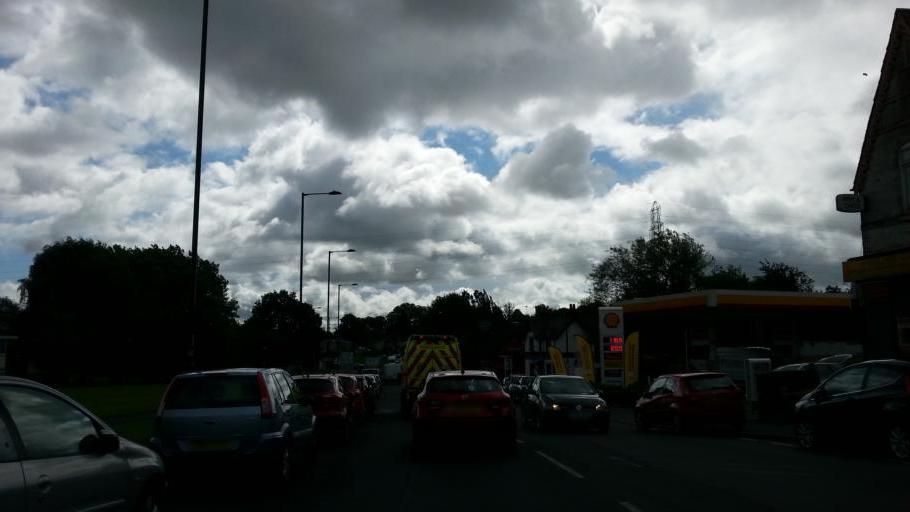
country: GB
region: England
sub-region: City and Borough of Birmingham
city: Bartley Green
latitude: 52.4479
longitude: -1.9462
